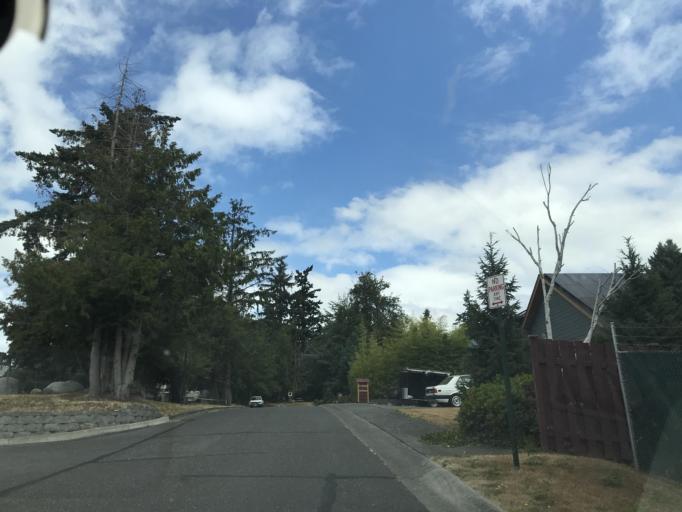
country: US
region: Washington
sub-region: Whatcom County
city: Bellingham
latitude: 48.7220
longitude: -122.4826
